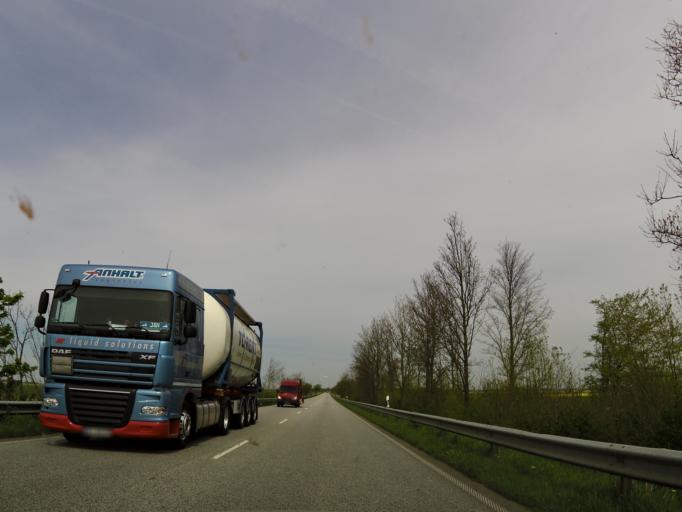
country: DE
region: Schleswig-Holstein
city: Norderwohrden
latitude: 54.2266
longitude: 9.0406
